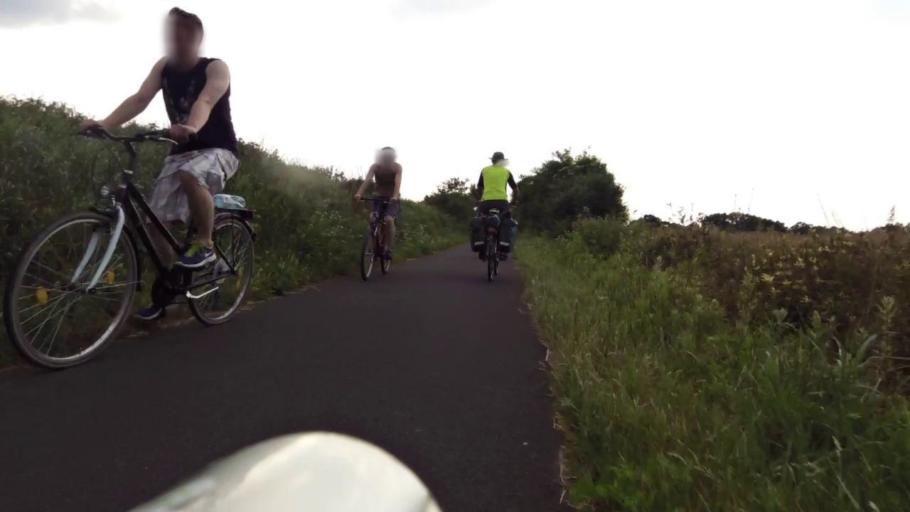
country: PL
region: Kujawsko-Pomorskie
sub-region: Powiat torunski
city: Lubianka
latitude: 53.1122
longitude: 18.5034
